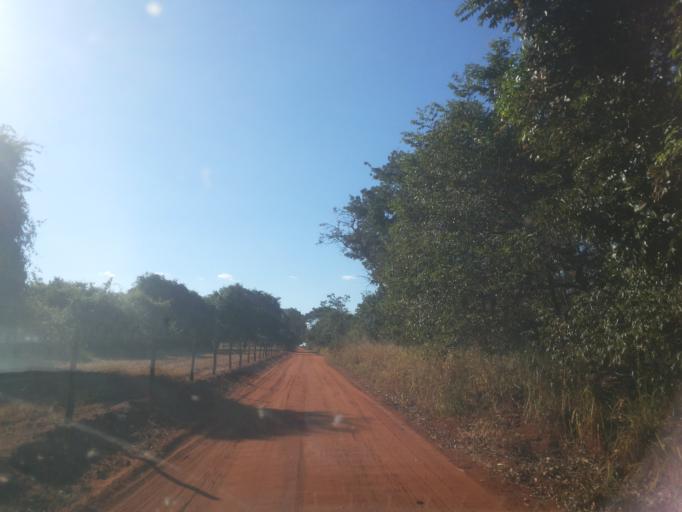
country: BR
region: Minas Gerais
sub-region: Centralina
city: Centralina
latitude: -18.7238
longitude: -49.1563
